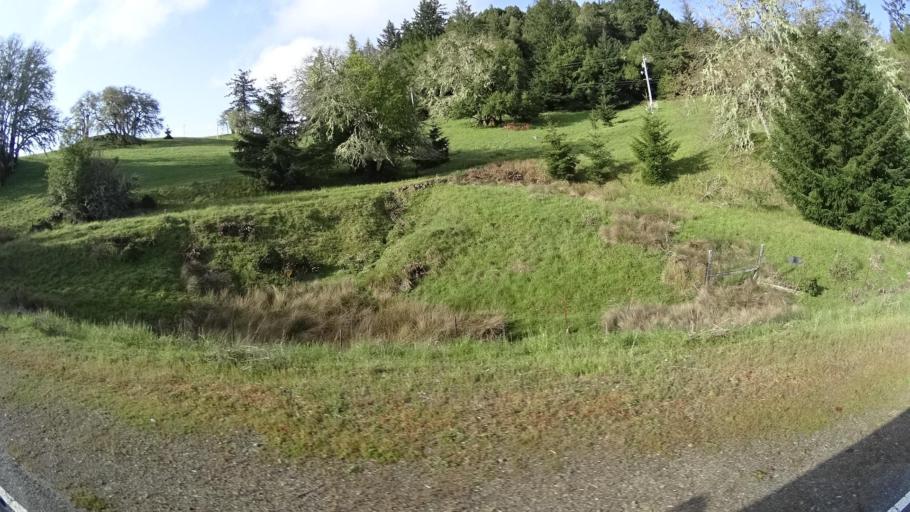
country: US
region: California
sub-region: Humboldt County
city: Blue Lake
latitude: 40.7381
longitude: -123.9493
